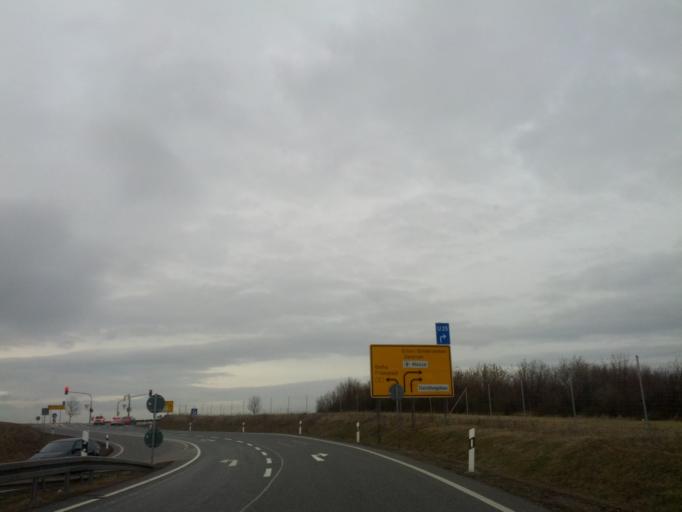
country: DE
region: Thuringia
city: Ingersleben
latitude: 50.9548
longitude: 10.9435
